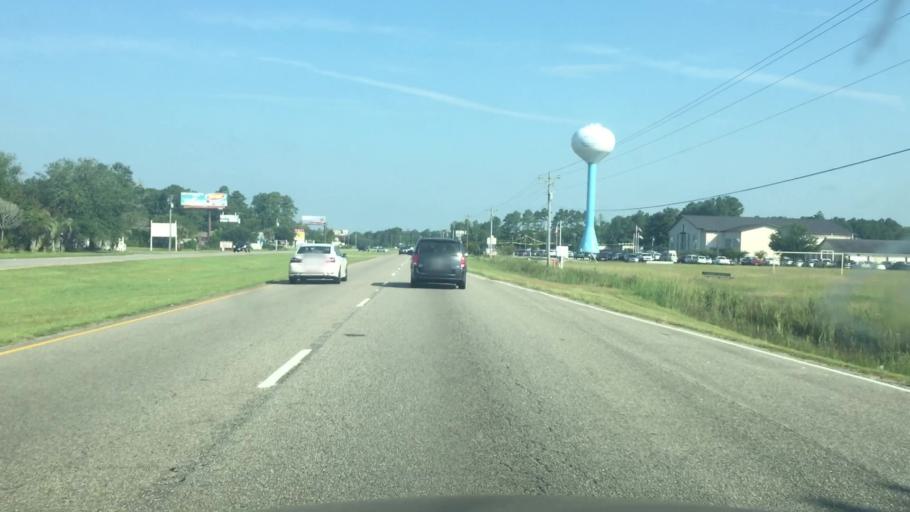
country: US
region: South Carolina
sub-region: Horry County
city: North Myrtle Beach
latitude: 33.8996
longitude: -78.6985
